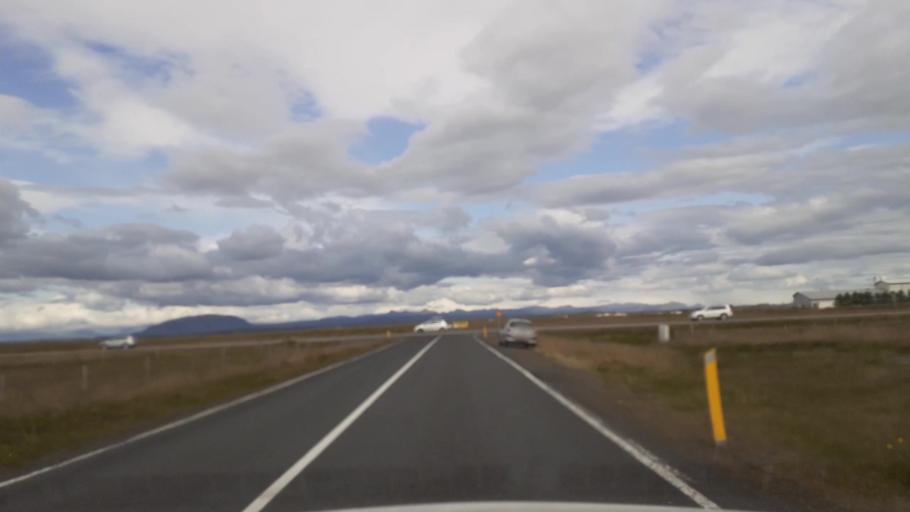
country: IS
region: South
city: Selfoss
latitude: 63.9429
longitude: -20.8383
